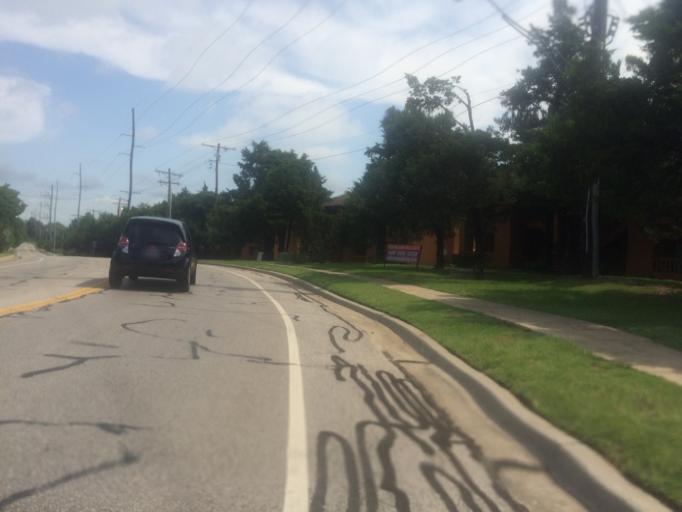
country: US
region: Oklahoma
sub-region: Cleveland County
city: Norman
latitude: 35.1828
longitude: -97.4237
